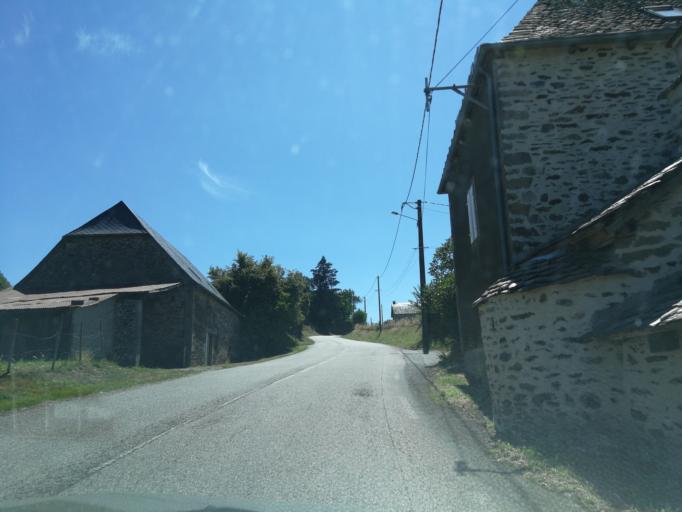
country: FR
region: Limousin
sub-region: Departement de la Correze
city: Argentat
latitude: 45.0453
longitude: 1.9503
